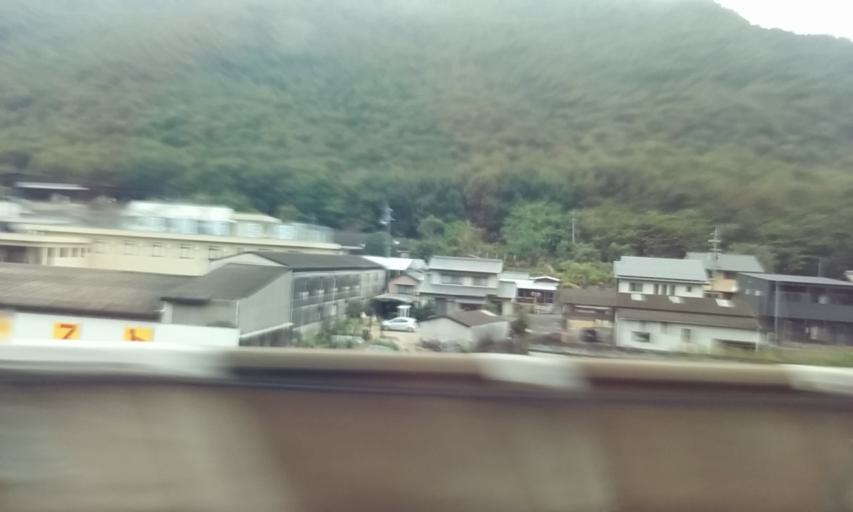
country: JP
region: Okayama
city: Okayama-shi
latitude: 34.7391
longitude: 134.1500
